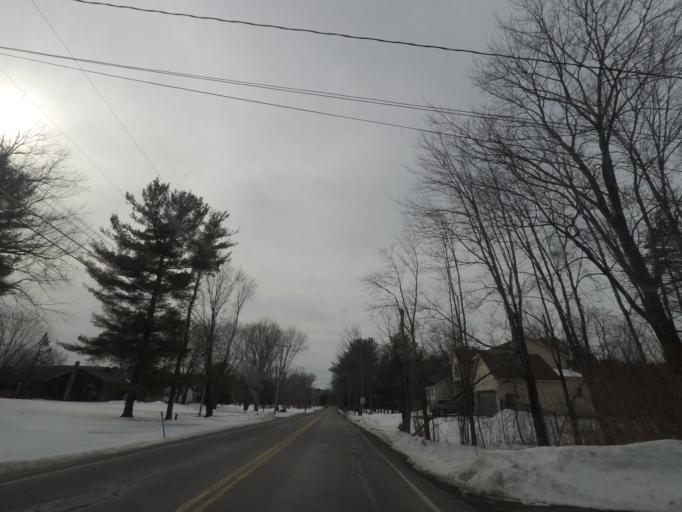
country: US
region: New York
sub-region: Albany County
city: Altamont
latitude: 42.6969
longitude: -73.9744
